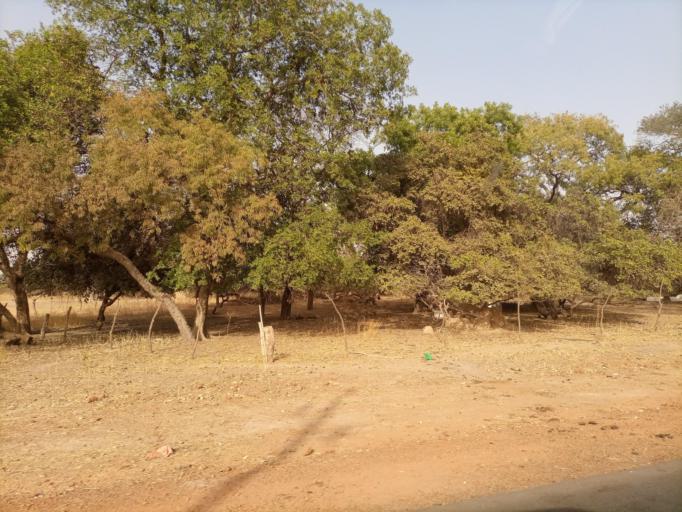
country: SN
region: Fatick
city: Passi
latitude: 14.0379
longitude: -16.3184
